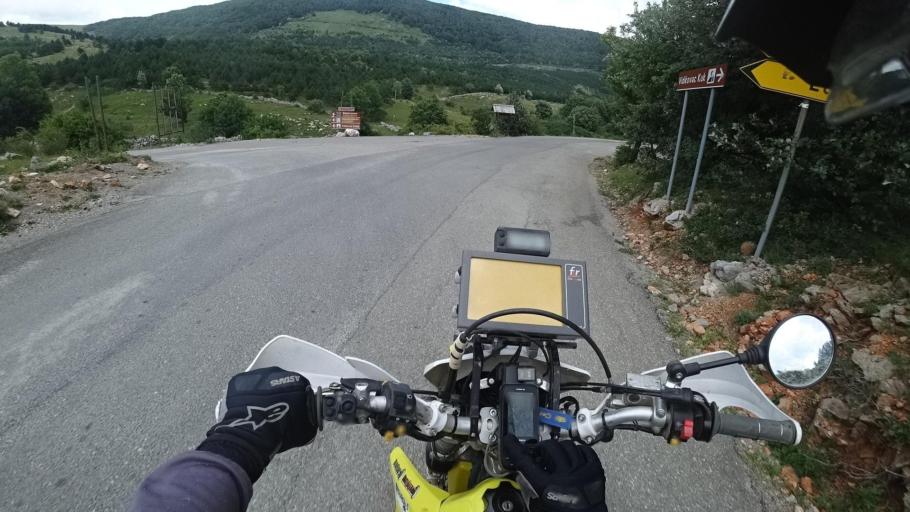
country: HR
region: Licko-Senjska
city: Senj
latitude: 45.1035
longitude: 14.9081
